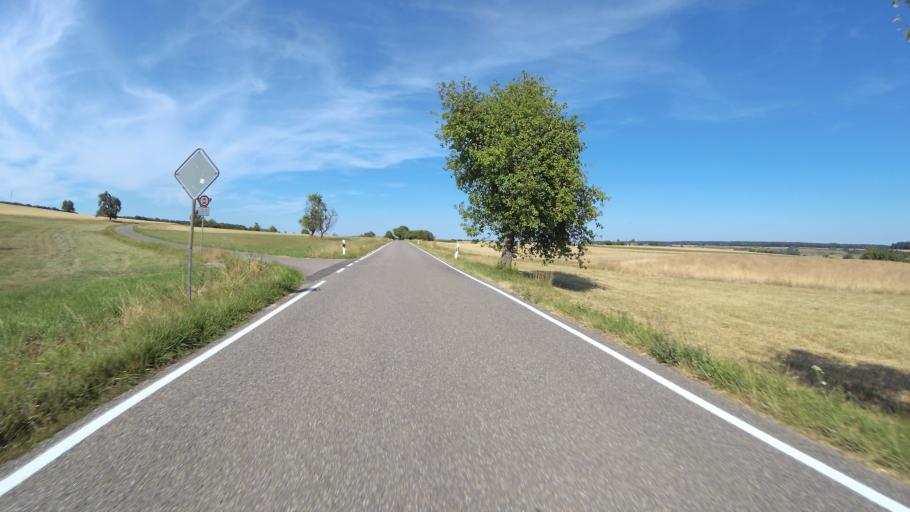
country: DE
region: Saarland
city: Gersheim
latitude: 49.1532
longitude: 7.2752
